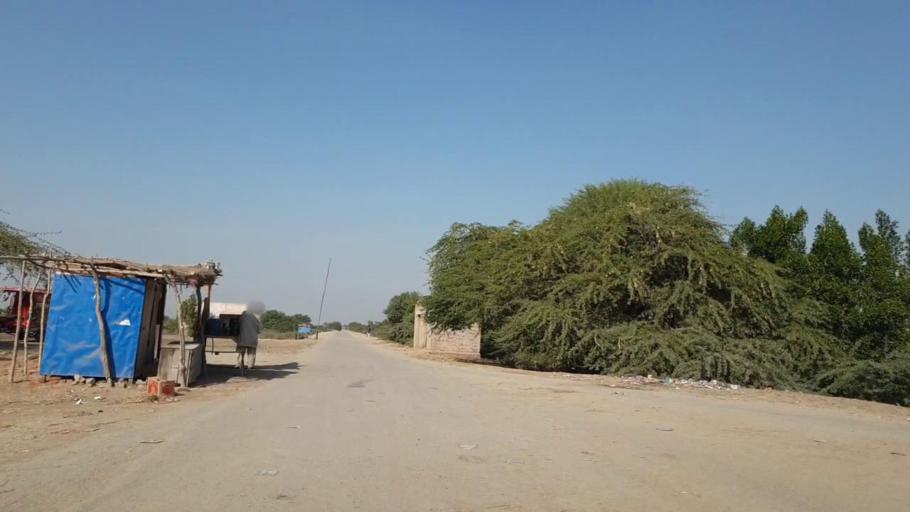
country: PK
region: Sindh
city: Digri
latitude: 25.0345
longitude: 69.1050
